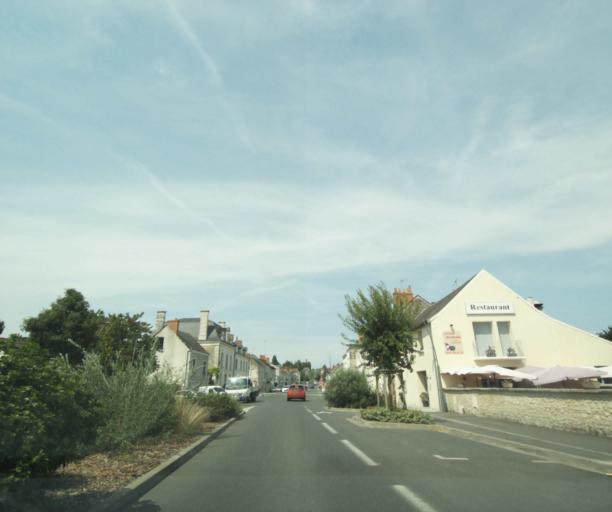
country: FR
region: Centre
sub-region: Departement d'Indre-et-Loire
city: Sainte-Maure-de-Touraine
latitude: 47.1097
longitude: 0.6148
